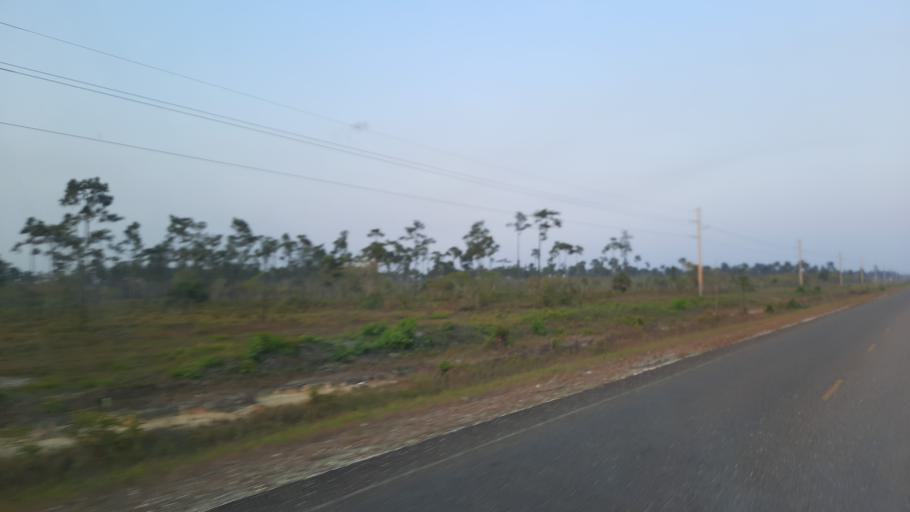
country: BZ
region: Stann Creek
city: Placencia
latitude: 16.5321
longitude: -88.4678
